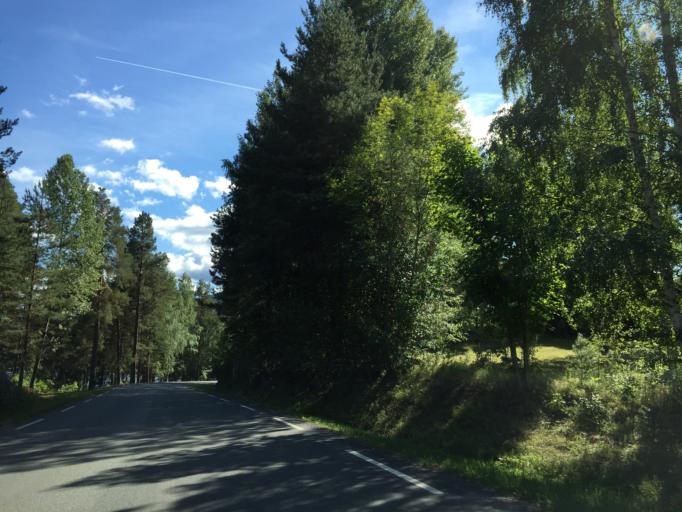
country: NO
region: Buskerud
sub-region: Ovre Eiker
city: Hokksund
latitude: 59.6991
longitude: 9.8440
